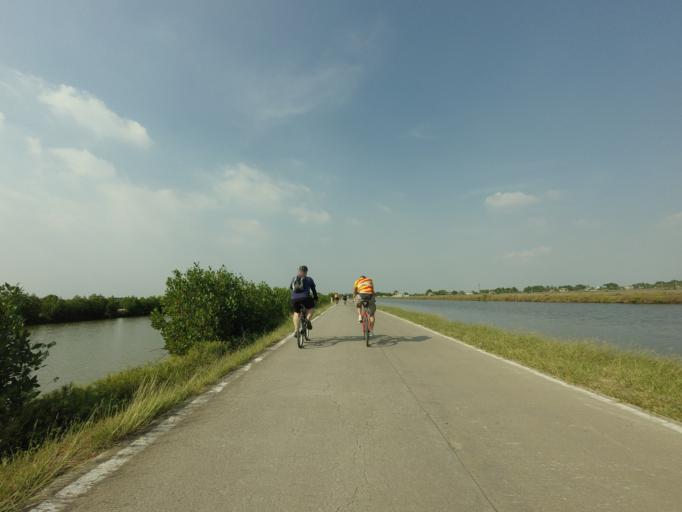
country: TH
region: Samut Sakhon
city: Samut Sakhon
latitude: 13.4944
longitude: 100.3614
